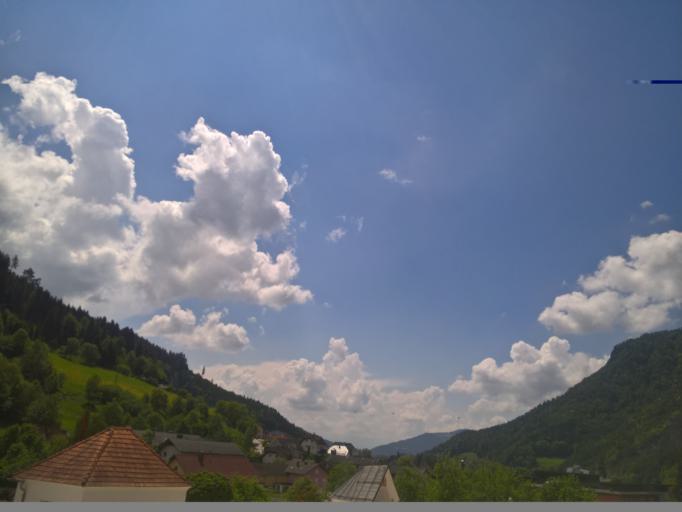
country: AT
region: Carinthia
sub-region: Politischer Bezirk Sankt Veit an der Glan
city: Eberstein
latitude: 46.8105
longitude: 14.5624
